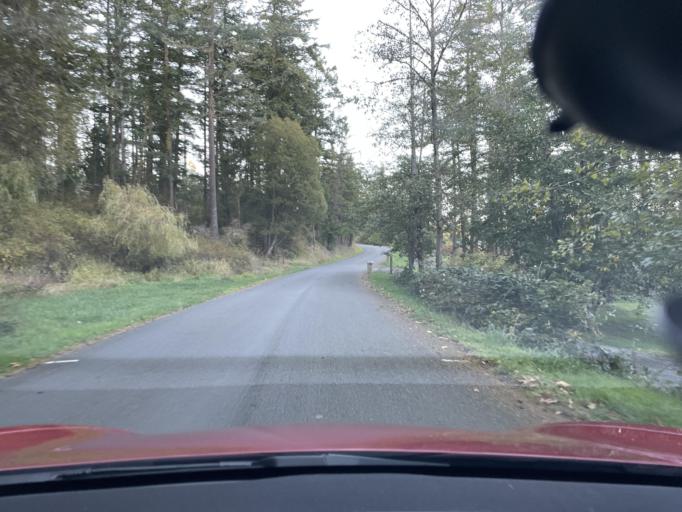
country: US
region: Washington
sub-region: San Juan County
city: Friday Harbor
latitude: 48.6052
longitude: -123.1481
